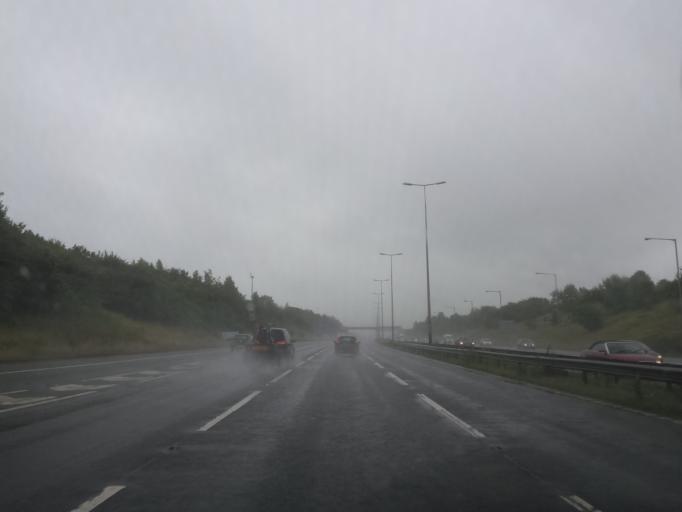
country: GB
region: England
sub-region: Leicestershire
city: Kirby Muxloe
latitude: 52.6353
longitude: -1.2174
